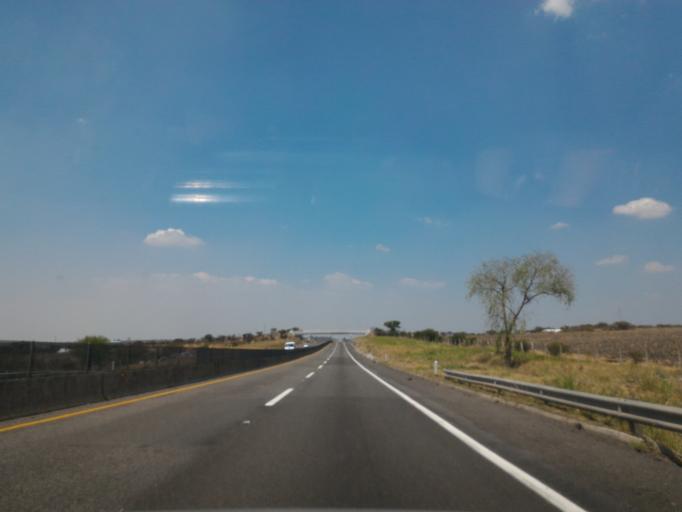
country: MX
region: Jalisco
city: Jalostotitlan
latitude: 21.0932
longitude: -102.4829
